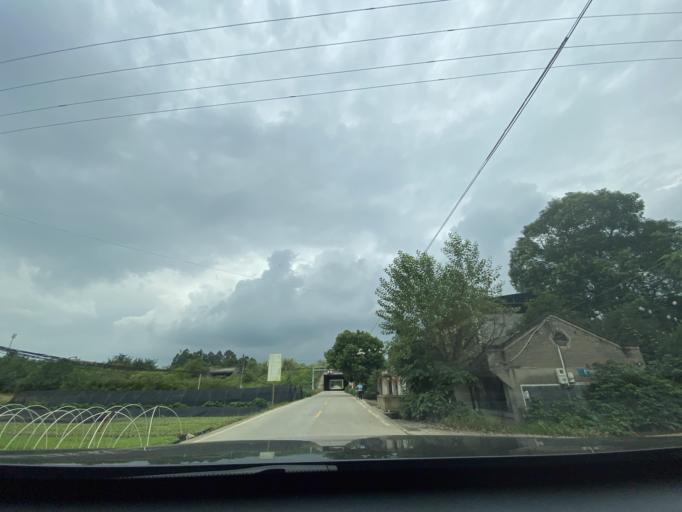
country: CN
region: Sichuan
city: Wujin
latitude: 30.3846
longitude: 103.9676
